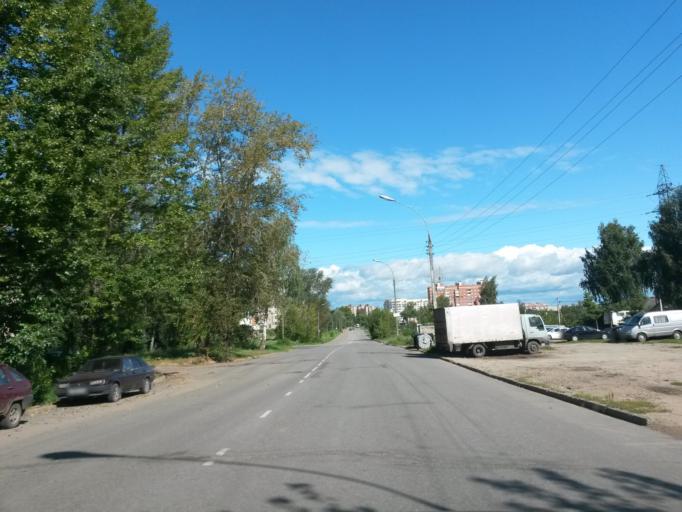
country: RU
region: Jaroslavl
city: Yaroslavl
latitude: 57.5820
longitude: 39.8658
